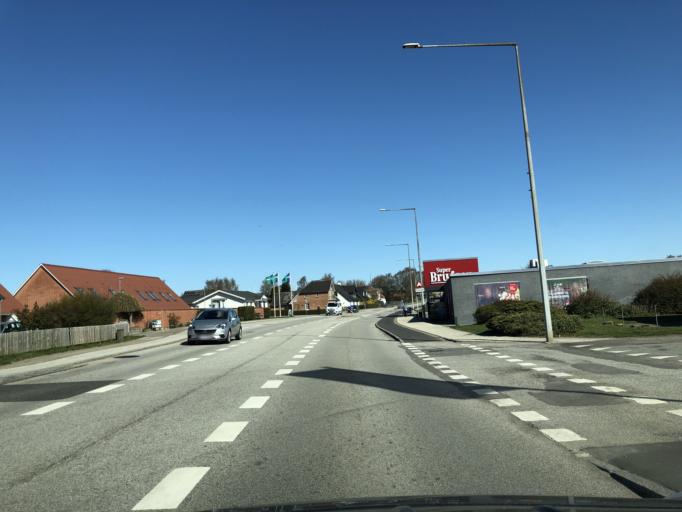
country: DK
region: North Denmark
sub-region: Rebild Kommune
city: Stovring
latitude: 56.8929
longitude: 9.8370
